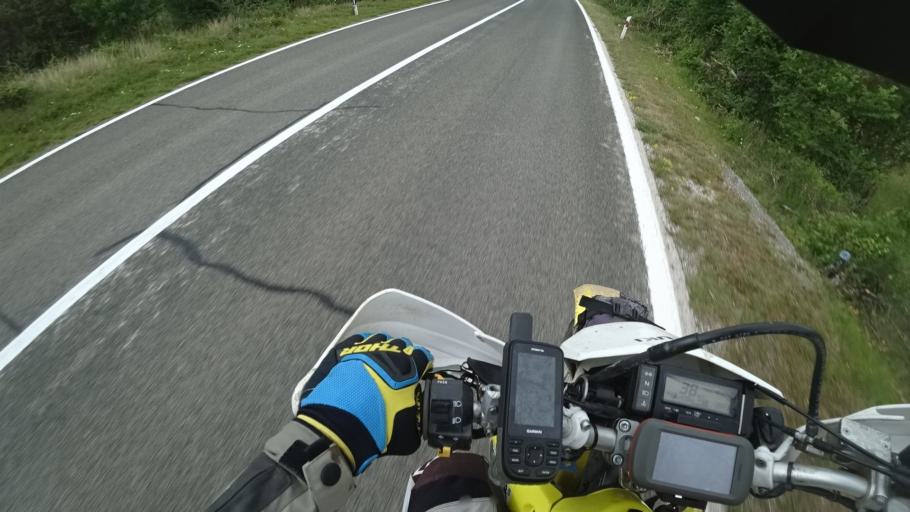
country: HR
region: Sibensko-Kniniska
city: Knin
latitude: 44.0152
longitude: 16.2707
